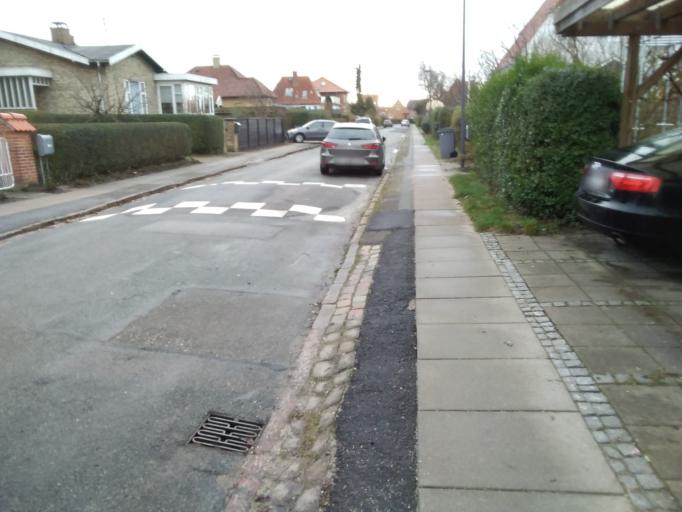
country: DK
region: Capital Region
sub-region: Tarnby Kommune
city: Tarnby
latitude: 55.6428
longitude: 12.6232
